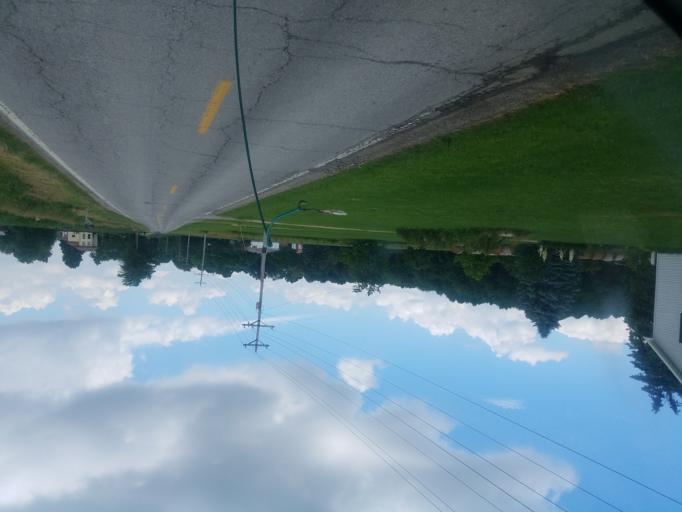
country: US
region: Ohio
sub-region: Huron County
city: Plymouth
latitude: 41.0408
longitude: -82.6086
